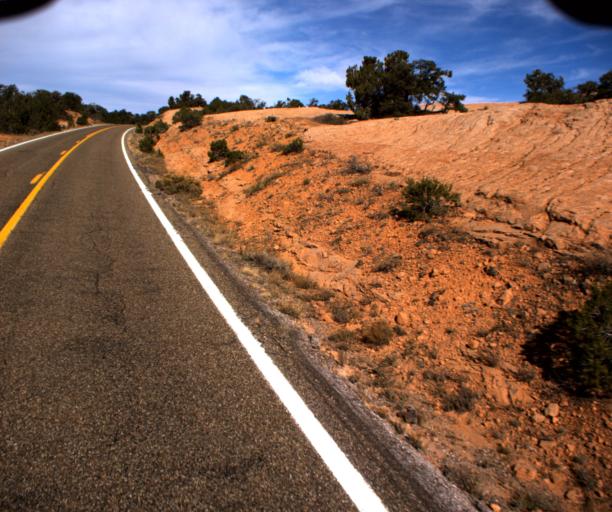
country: US
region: Arizona
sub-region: Navajo County
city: Kayenta
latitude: 36.6445
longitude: -110.5161
